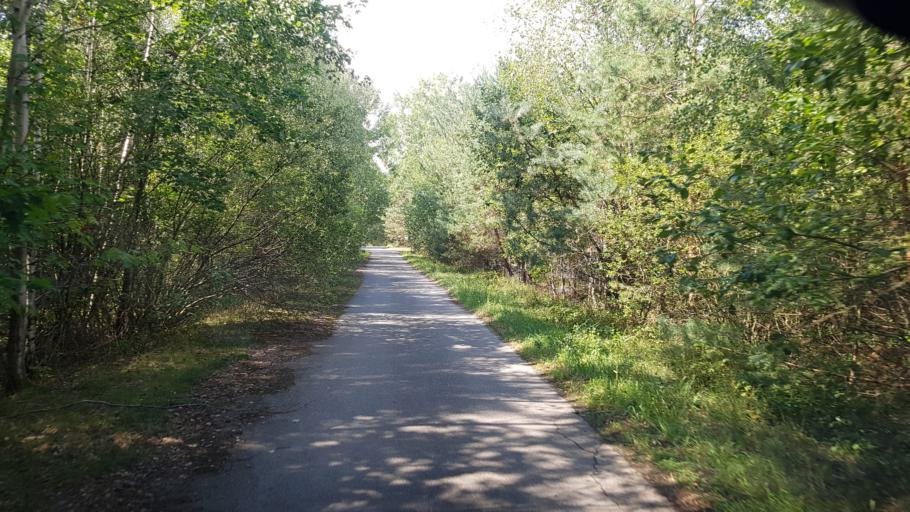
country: DE
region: Brandenburg
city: Calau
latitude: 51.7770
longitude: 13.9481
